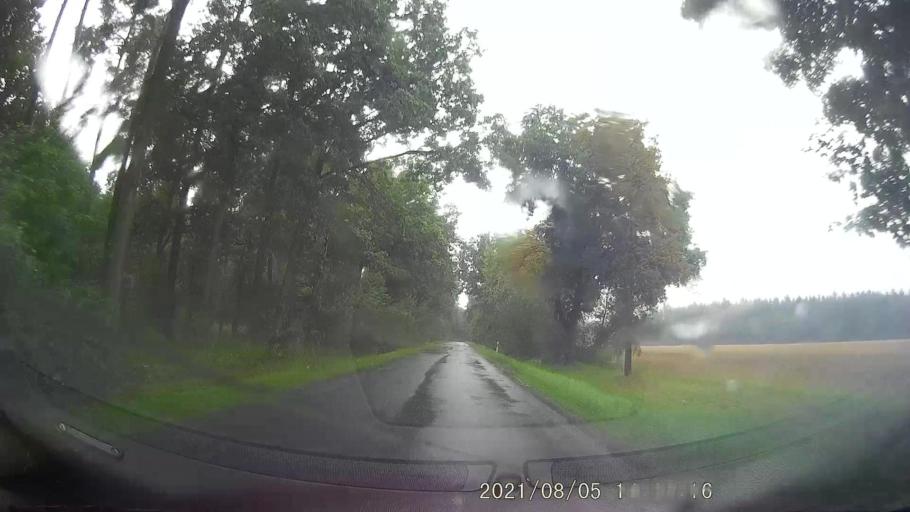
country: PL
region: Opole Voivodeship
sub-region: Powiat nyski
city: Sidzina
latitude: 50.4665
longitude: 17.4765
